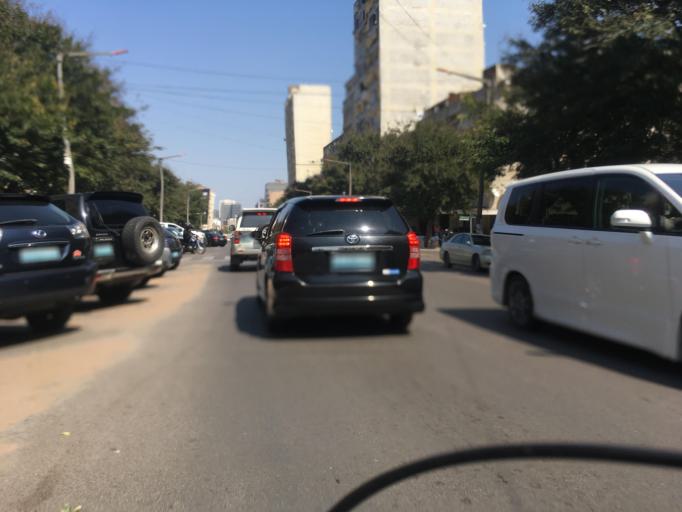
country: MZ
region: Maputo City
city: Maputo
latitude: -25.9634
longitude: 32.5729
